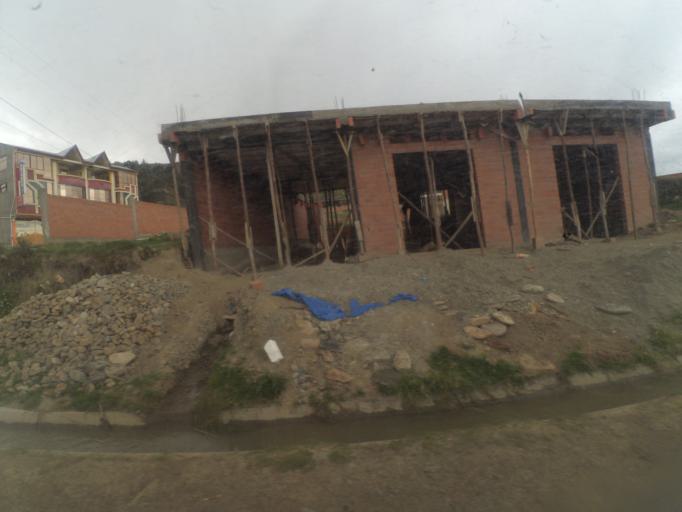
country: BO
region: La Paz
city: La Paz
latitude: -16.5723
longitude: -68.1770
